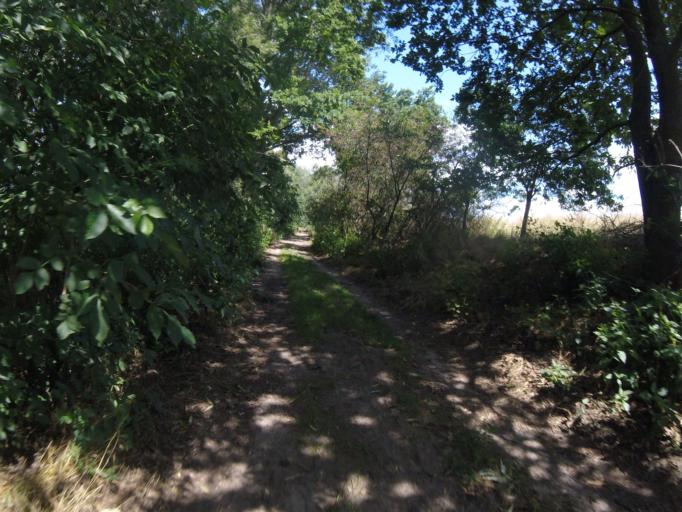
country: DE
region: Brandenburg
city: Mittenwalde
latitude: 52.2596
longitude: 13.5909
